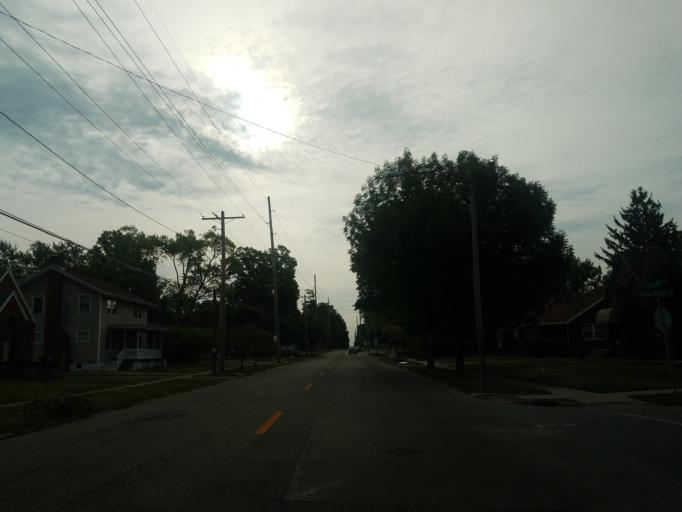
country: US
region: Illinois
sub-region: McLean County
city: Bloomington
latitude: 40.4739
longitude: -88.9715
